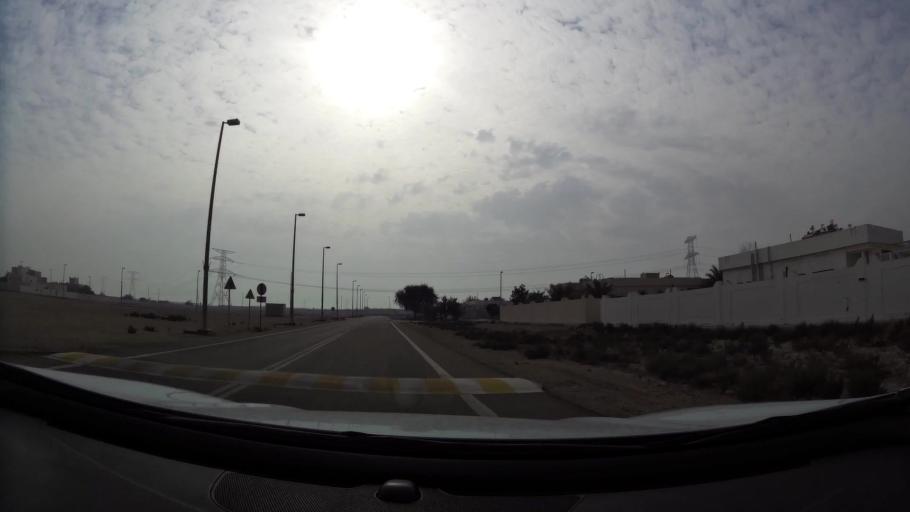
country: AE
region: Abu Dhabi
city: Abu Dhabi
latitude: 24.6568
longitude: 54.7650
